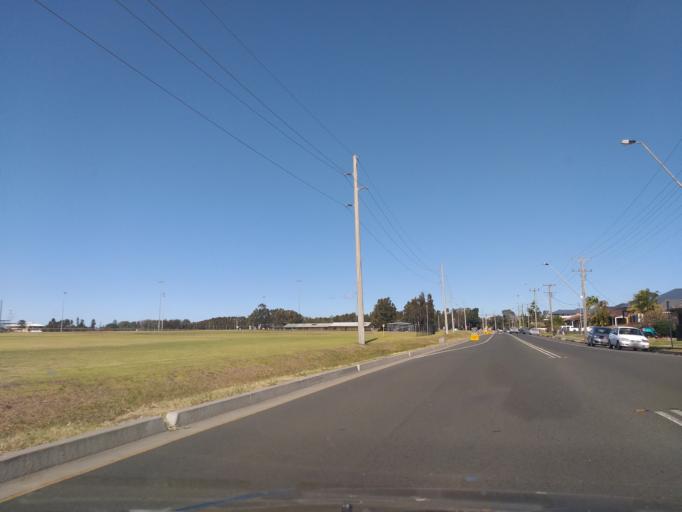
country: AU
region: New South Wales
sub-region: Wollongong
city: Fairy Meadow
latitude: -34.3926
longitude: 150.9016
